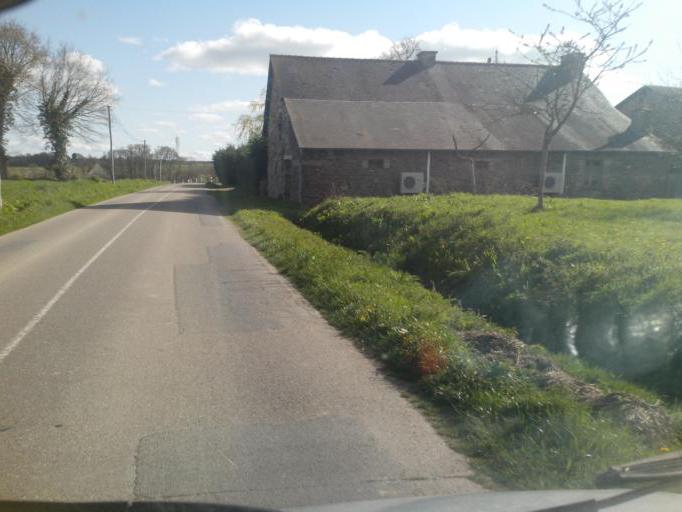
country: FR
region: Brittany
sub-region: Departement d'Ille-et-Vilaine
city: Maxent
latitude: 47.9764
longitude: -2.0224
